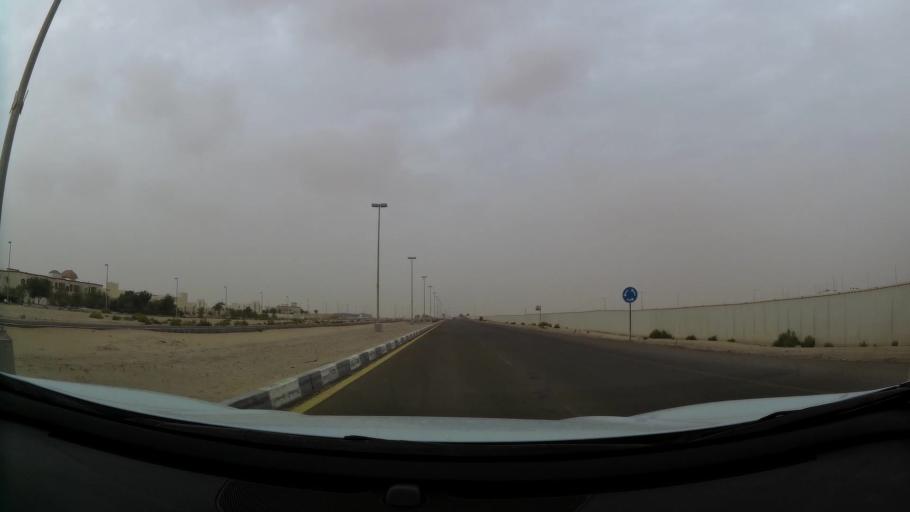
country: AE
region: Abu Dhabi
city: Abu Dhabi
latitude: 24.4266
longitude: 54.7180
